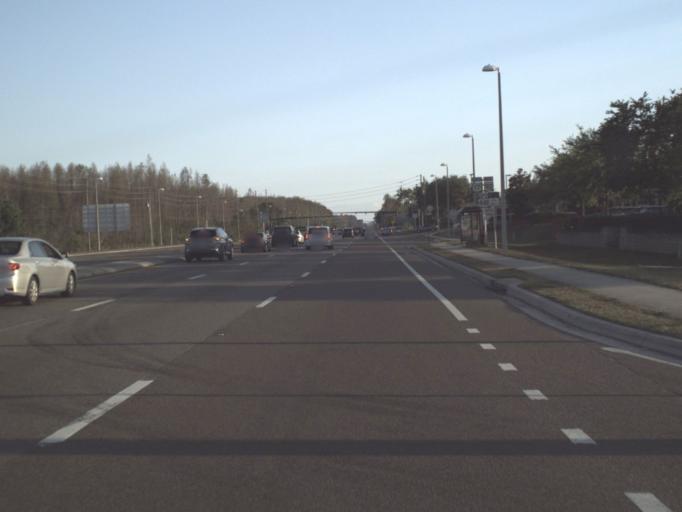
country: US
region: Florida
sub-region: Orange County
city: Hunters Creek
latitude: 28.3713
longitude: -81.4046
